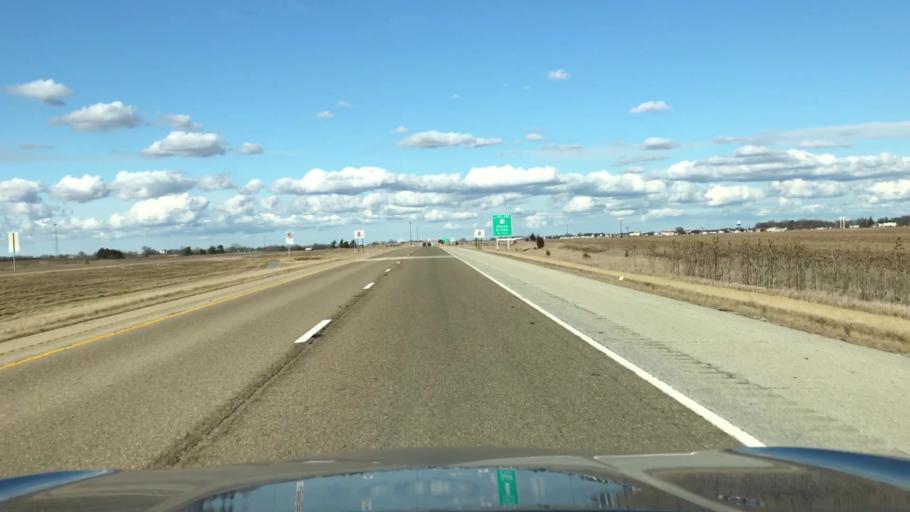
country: US
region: Illinois
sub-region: McLean County
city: Chenoa
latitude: 40.7281
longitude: -88.7371
